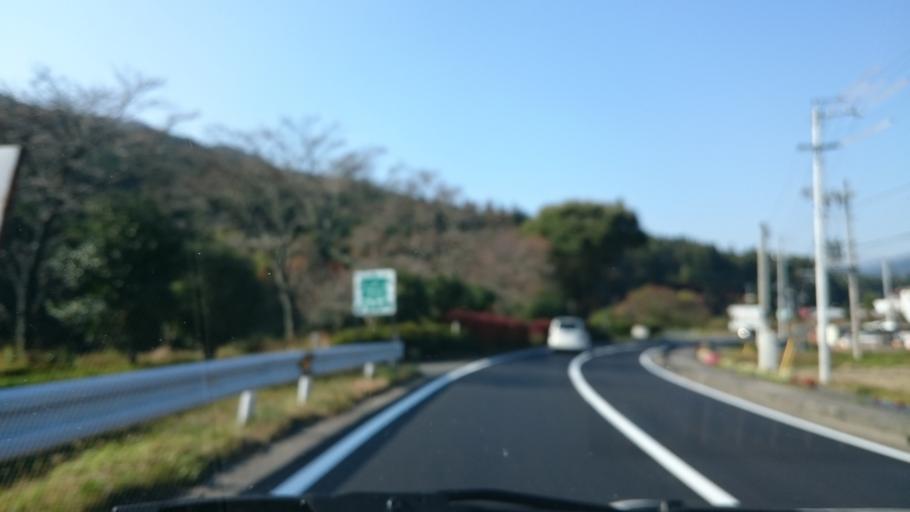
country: JP
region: Gifu
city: Nakatsugawa
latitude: 35.6935
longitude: 137.3815
